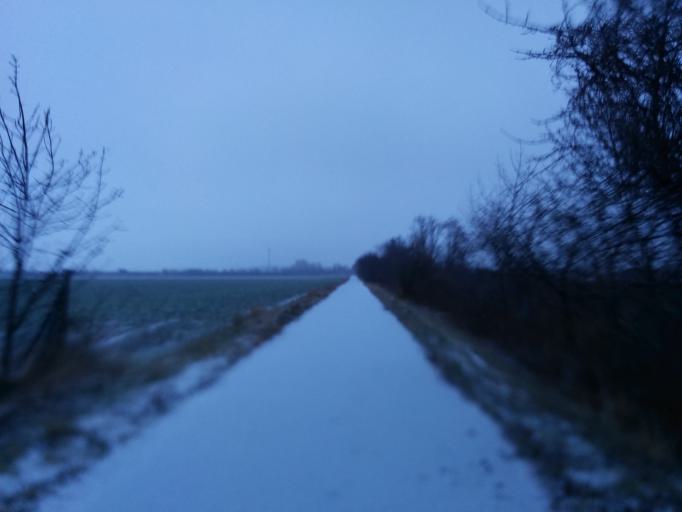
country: AT
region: Lower Austria
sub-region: Politischer Bezirk Baden
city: Trumau
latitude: 48.0091
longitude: 16.3603
